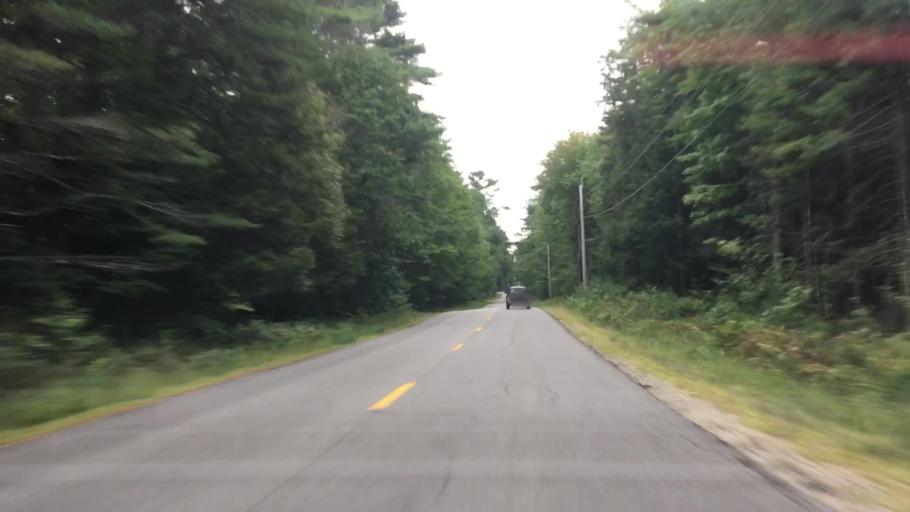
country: US
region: Maine
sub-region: Cumberland County
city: Freeport
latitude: 43.8790
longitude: -70.1572
